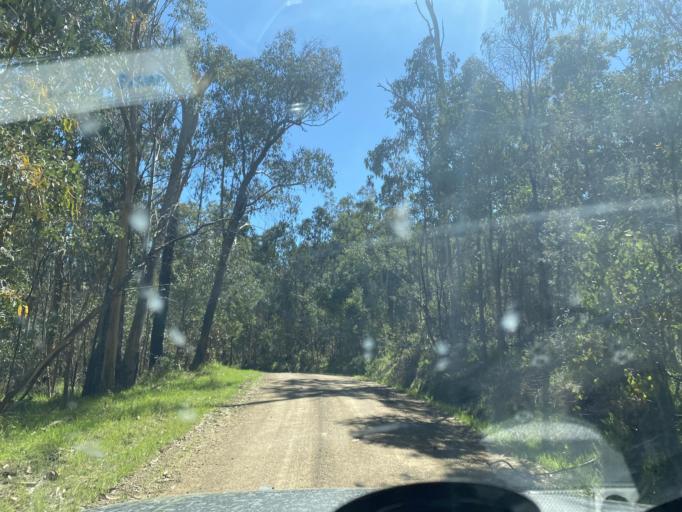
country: AU
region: Victoria
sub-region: Benalla
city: Benalla
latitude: -36.6968
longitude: 146.1777
